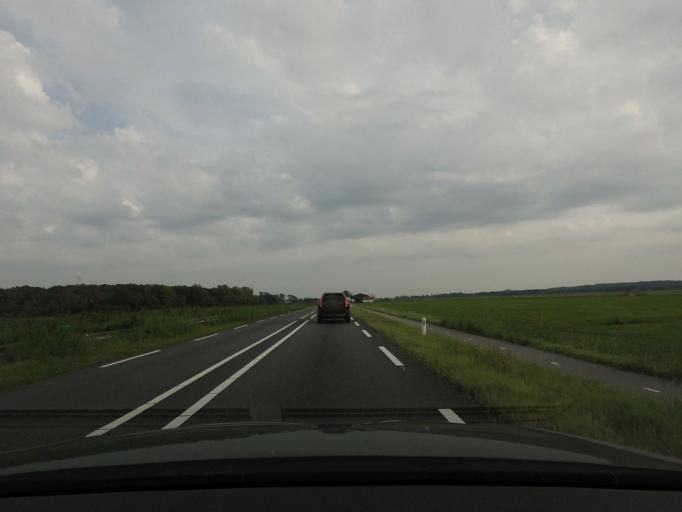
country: NL
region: North Holland
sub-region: Gemeente Schagen
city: Harenkarspel
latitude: 52.7291
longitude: 4.6941
